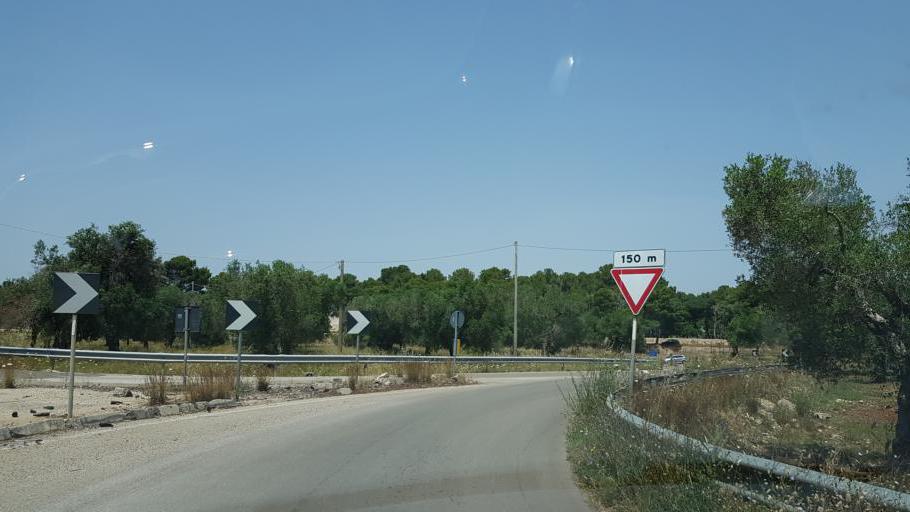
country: IT
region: Apulia
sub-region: Provincia di Lecce
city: Porto Cesareo
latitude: 40.2669
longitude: 17.9124
